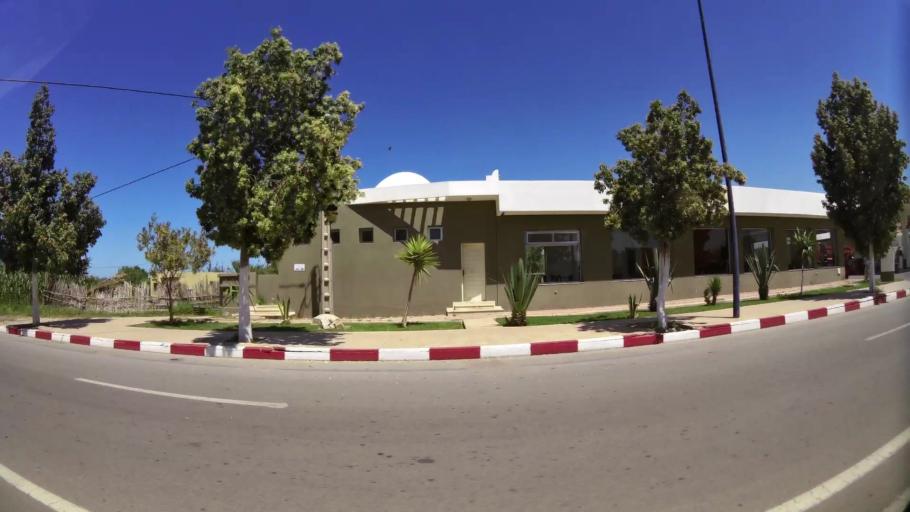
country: MA
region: Oriental
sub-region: Berkane-Taourirt
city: Madagh
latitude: 35.0686
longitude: -2.2168
